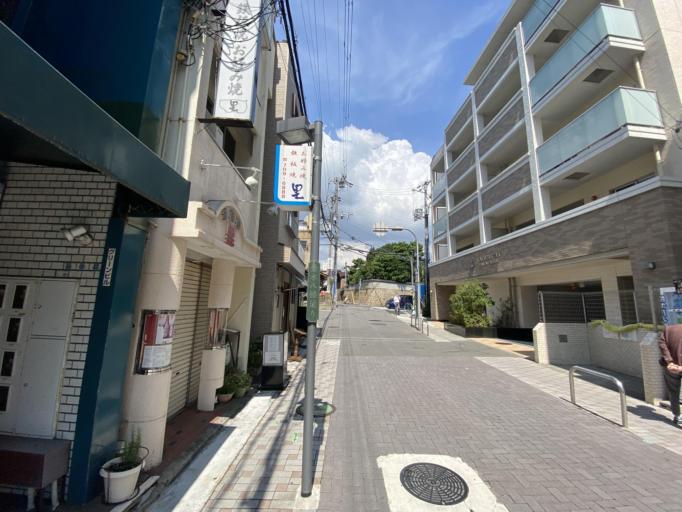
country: JP
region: Hyogo
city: Akashi
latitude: 34.6318
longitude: 135.0555
